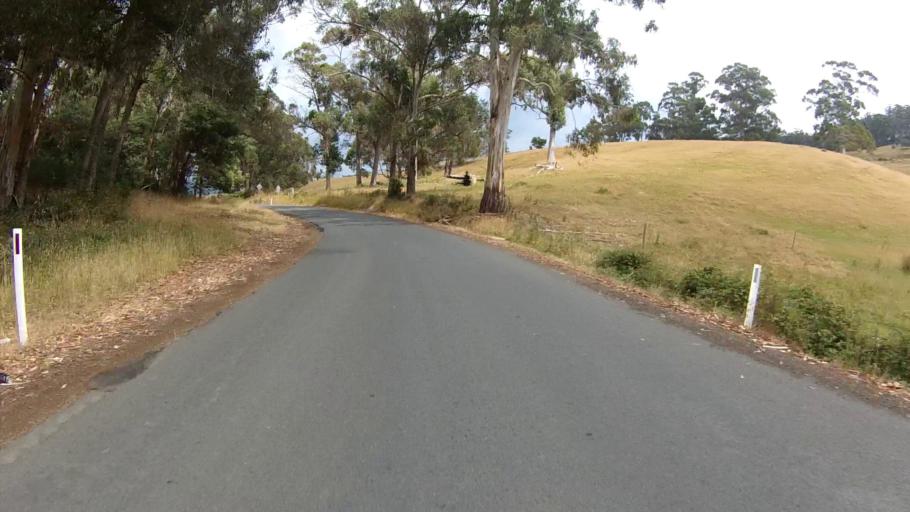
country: AU
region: Tasmania
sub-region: Huon Valley
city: Cygnet
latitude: -43.1811
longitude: 147.1137
